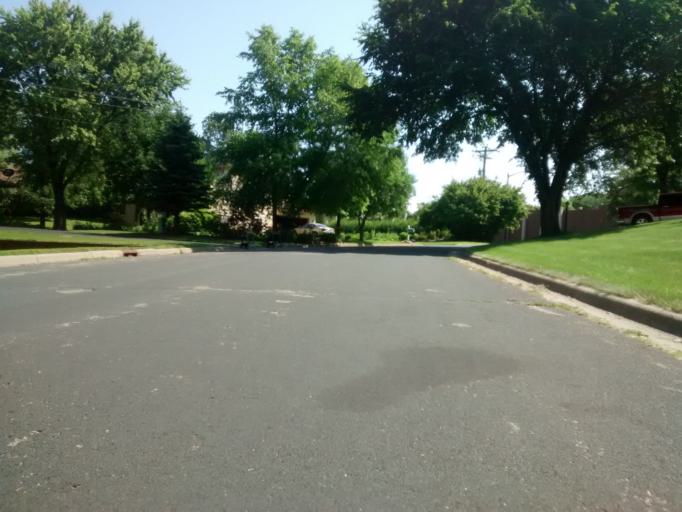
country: US
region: Minnesota
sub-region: Dakota County
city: Burnsville
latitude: 44.7606
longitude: -93.2905
